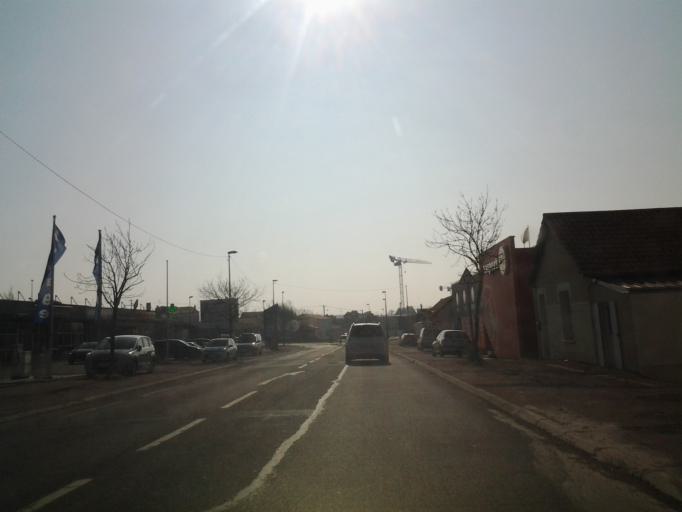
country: FR
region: Pays de la Loire
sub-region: Departement de la Vendee
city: Les Sables-d'Olonne
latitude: 46.5074
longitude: -1.7702
